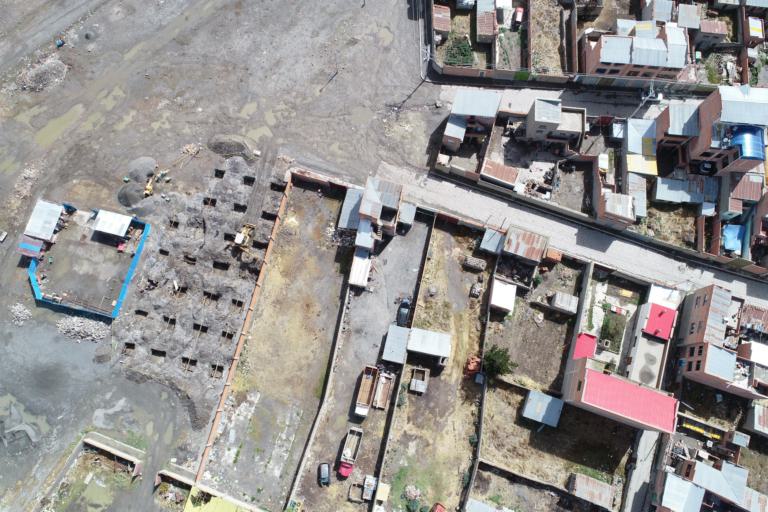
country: BO
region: La Paz
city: Achacachi
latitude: -16.0398
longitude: -68.6876
